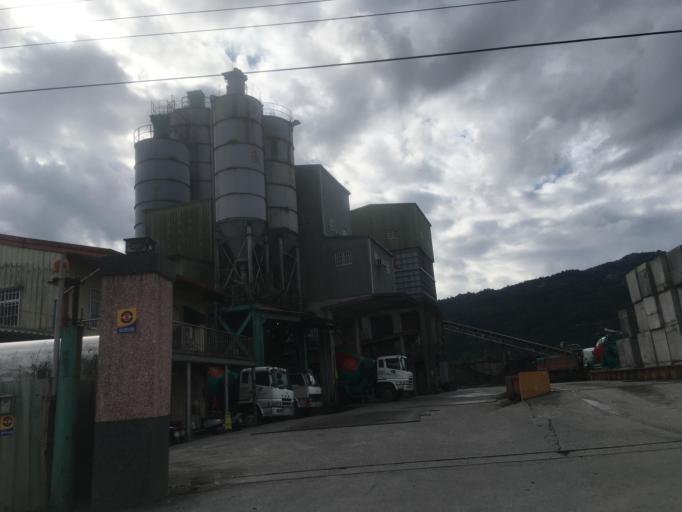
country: TW
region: Taiwan
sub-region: Yilan
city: Yilan
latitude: 24.6707
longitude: 121.6642
